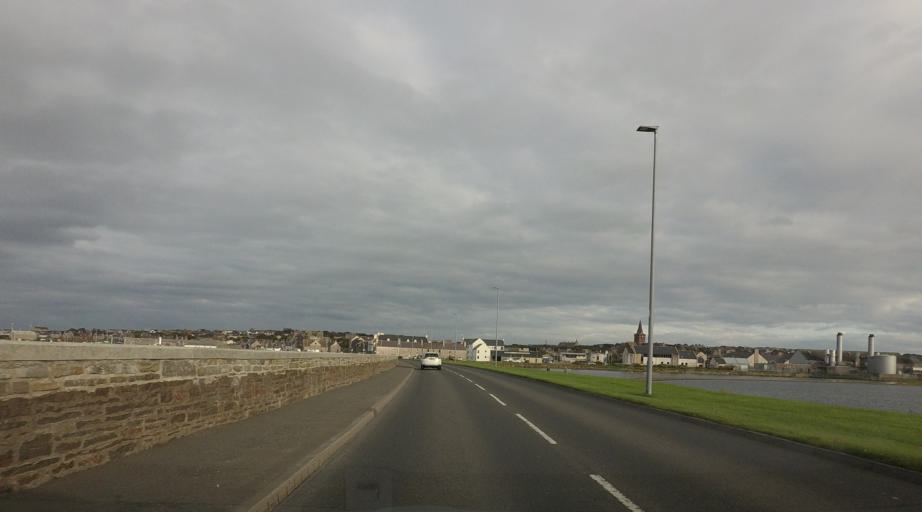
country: GB
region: Scotland
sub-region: Orkney Islands
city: Orkney
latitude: 58.9851
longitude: -2.9675
